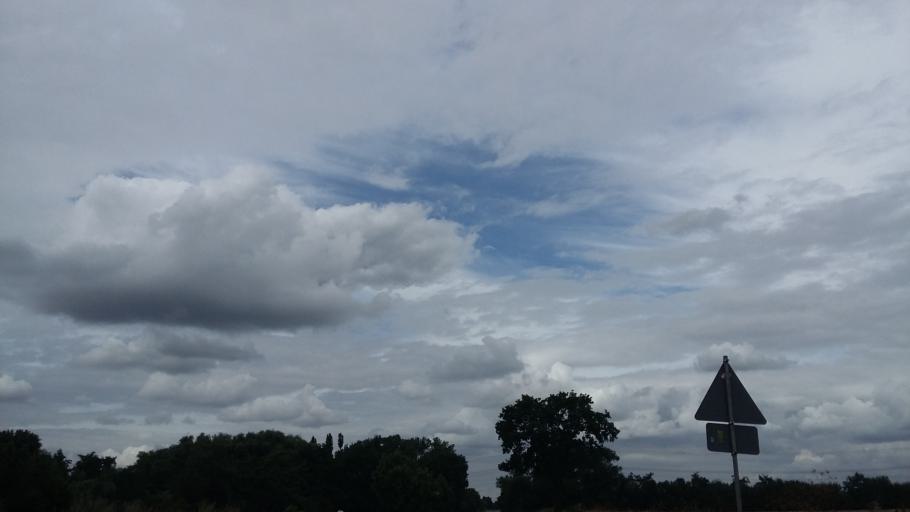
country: DE
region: Lower Saxony
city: Sarstedt
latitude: 52.2609
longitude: 9.8561
